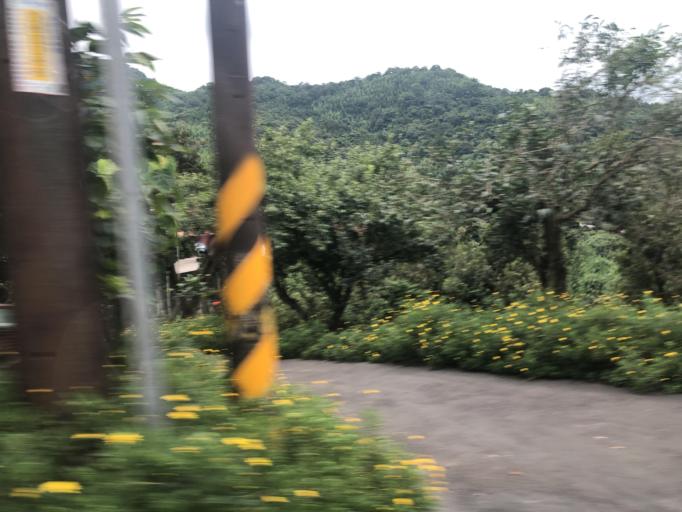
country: TW
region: Taiwan
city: Daxi
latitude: 24.8803
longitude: 121.4194
